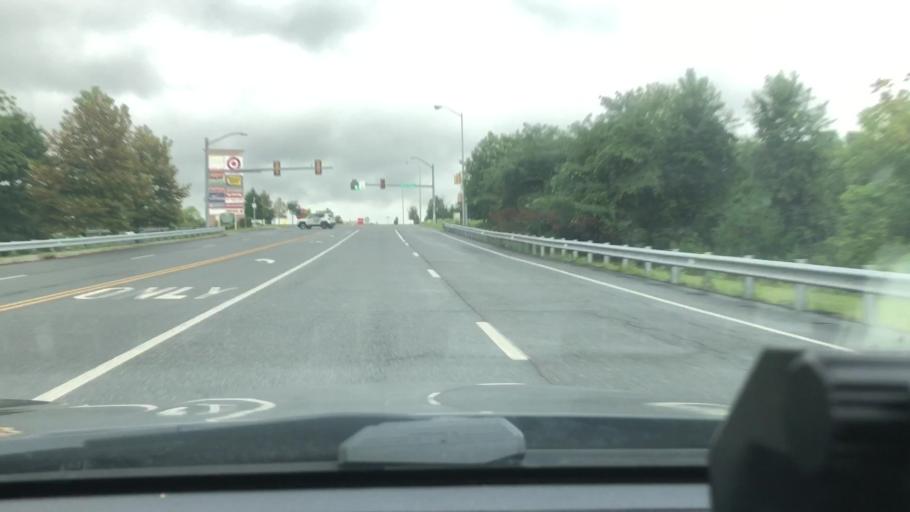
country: US
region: Pennsylvania
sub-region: Montgomery County
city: Halfway House
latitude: 40.2669
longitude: -75.6516
